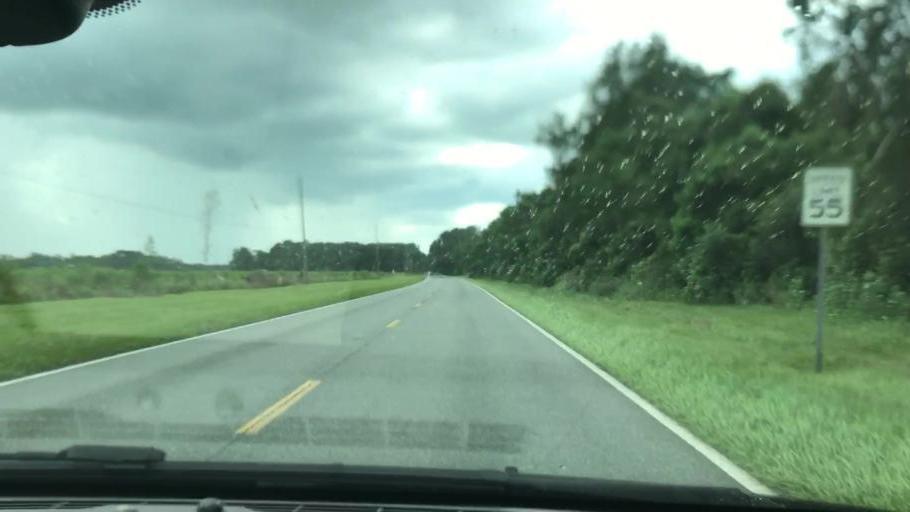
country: US
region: Florida
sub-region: Madison County
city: Madison
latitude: 30.4092
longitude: -83.3002
